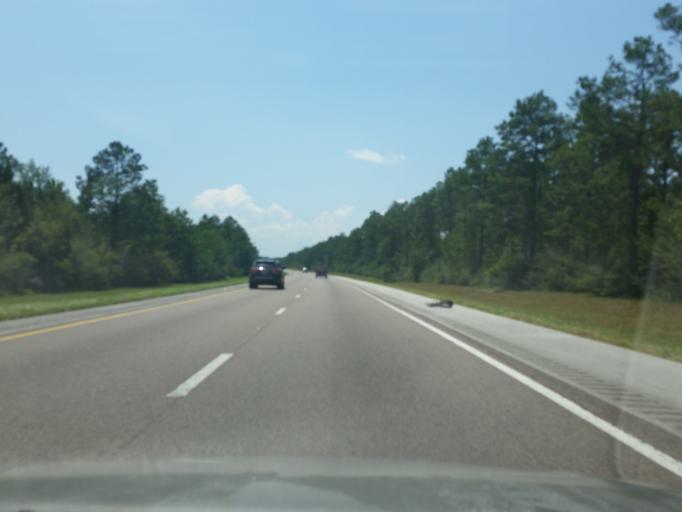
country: US
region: Florida
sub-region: Escambia County
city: Cantonment
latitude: 30.5786
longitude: -87.4401
